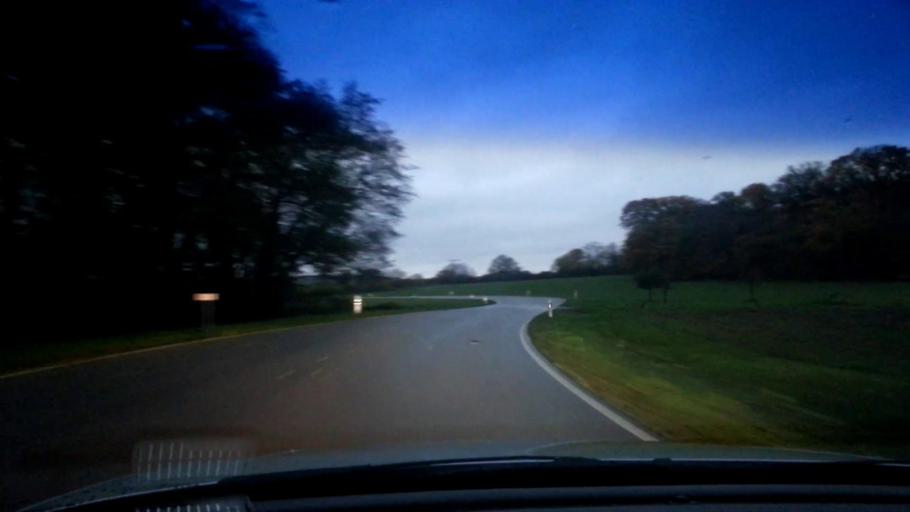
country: DE
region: Bavaria
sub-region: Upper Franconia
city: Schesslitz
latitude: 49.9544
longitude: 11.0263
